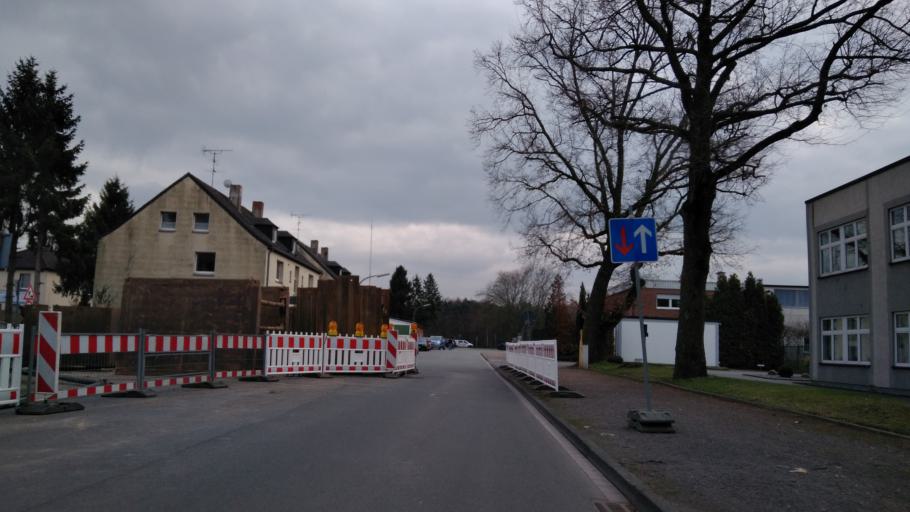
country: DE
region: North Rhine-Westphalia
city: Dorsten
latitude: 51.6590
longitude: 7.0031
